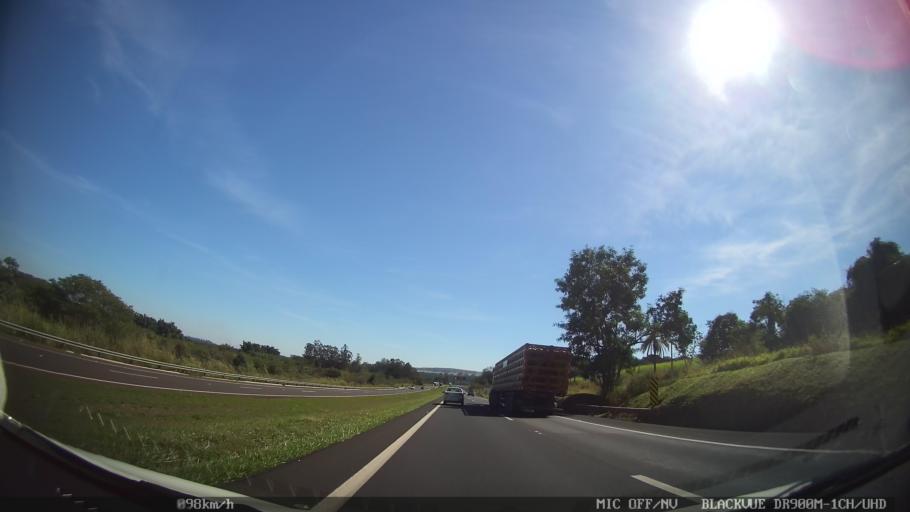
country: BR
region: Sao Paulo
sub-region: Santa Rita Do Passa Quatro
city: Santa Rita do Passa Quatro
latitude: -21.7444
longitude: -47.5763
